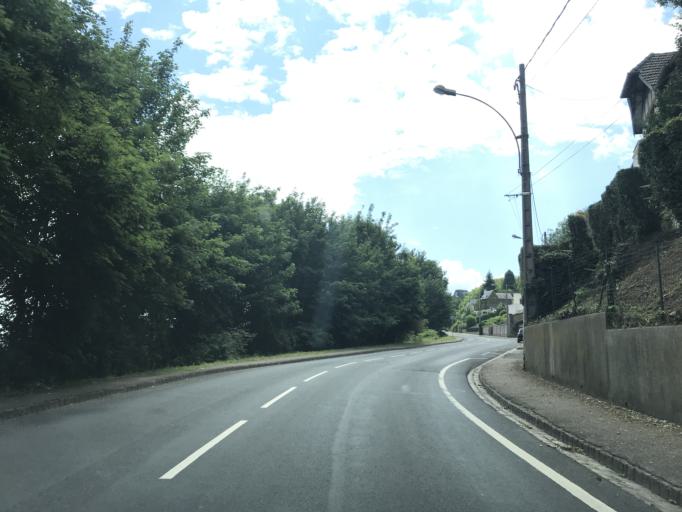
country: FR
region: Haute-Normandie
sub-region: Departement de la Seine-Maritime
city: Mont-Saint-Aignan
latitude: 49.4604
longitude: 1.0857
